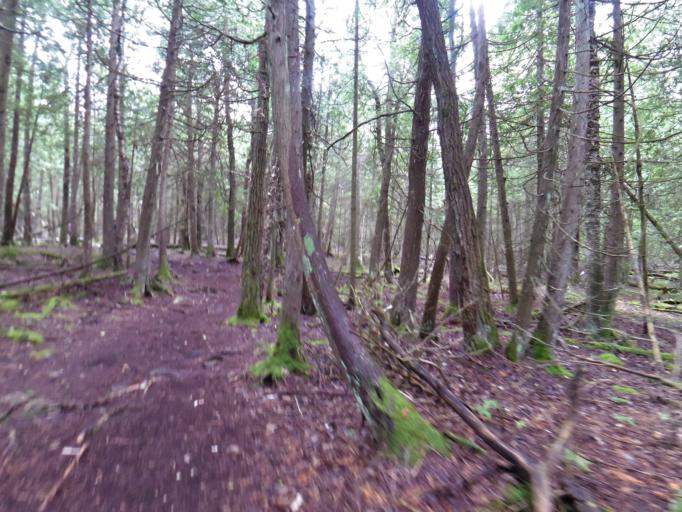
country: CA
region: Ontario
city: Tobermory
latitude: 45.2606
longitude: -81.6492
